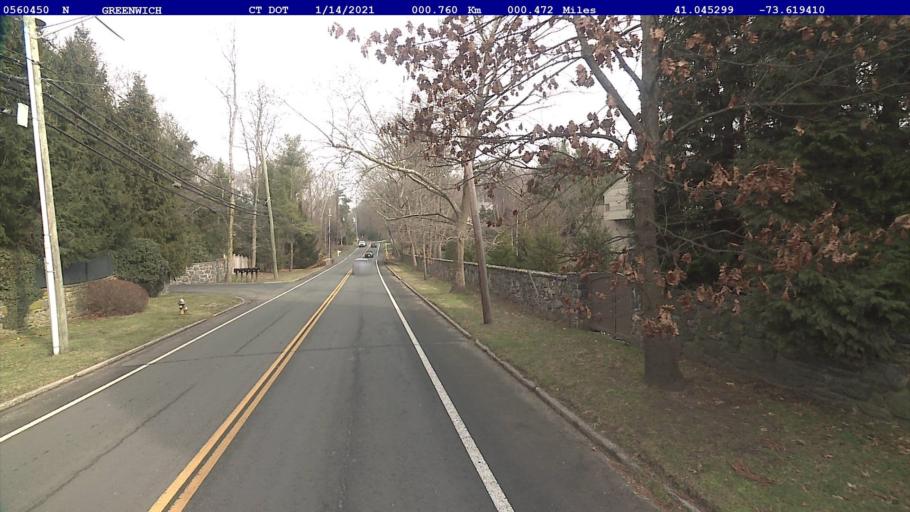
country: US
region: Connecticut
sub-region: Fairfield County
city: Greenwich
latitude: 41.0453
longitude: -73.6194
